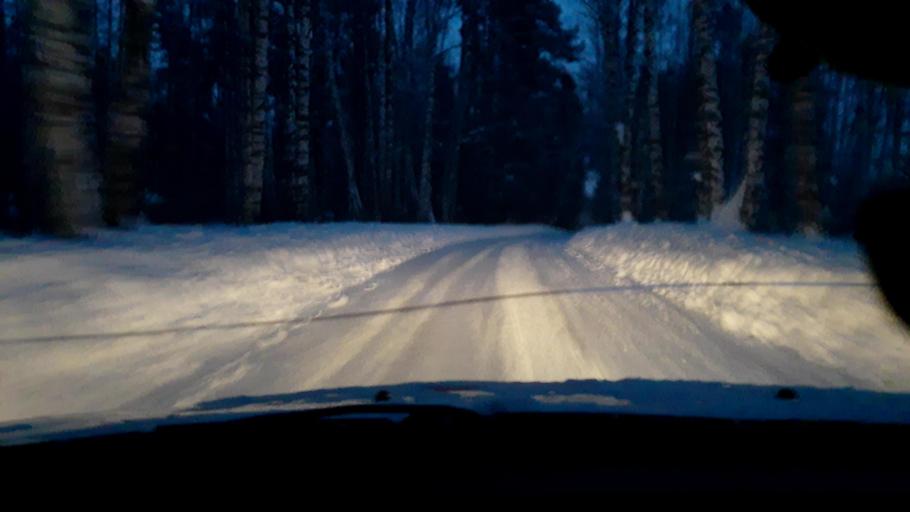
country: RU
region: Nizjnij Novgorod
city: Afonino
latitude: 56.1728
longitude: 44.0609
